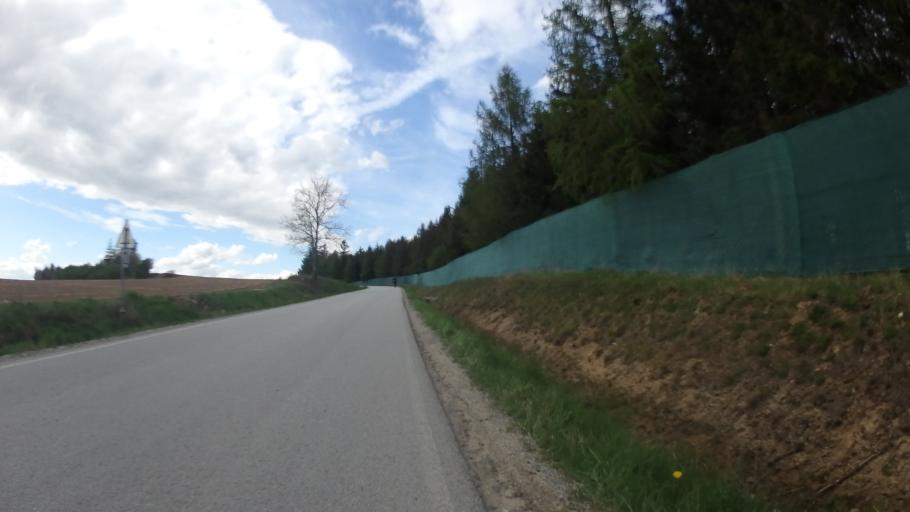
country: CZ
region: Vysocina
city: Merin
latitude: 49.3655
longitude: 15.9008
